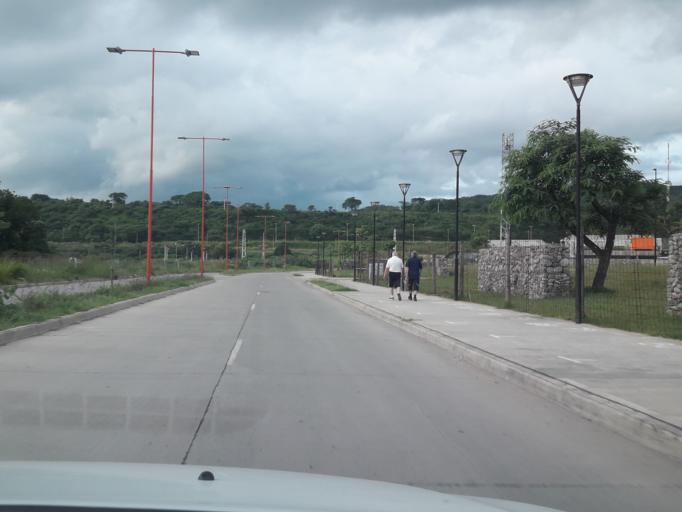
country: AR
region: Jujuy
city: San Salvador de Jujuy
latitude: -24.1820
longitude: -65.3280
